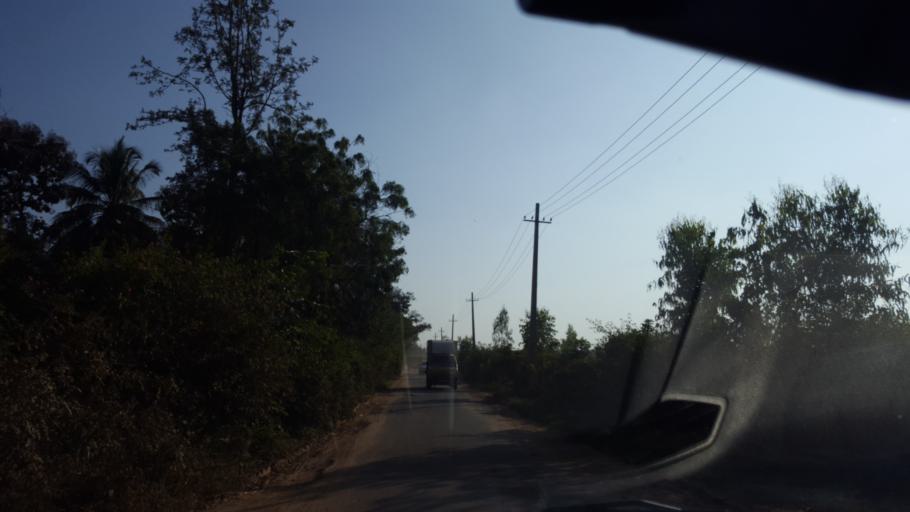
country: IN
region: Karnataka
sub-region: Bangalore Rural
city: Hoskote
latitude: 12.9285
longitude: 77.7571
